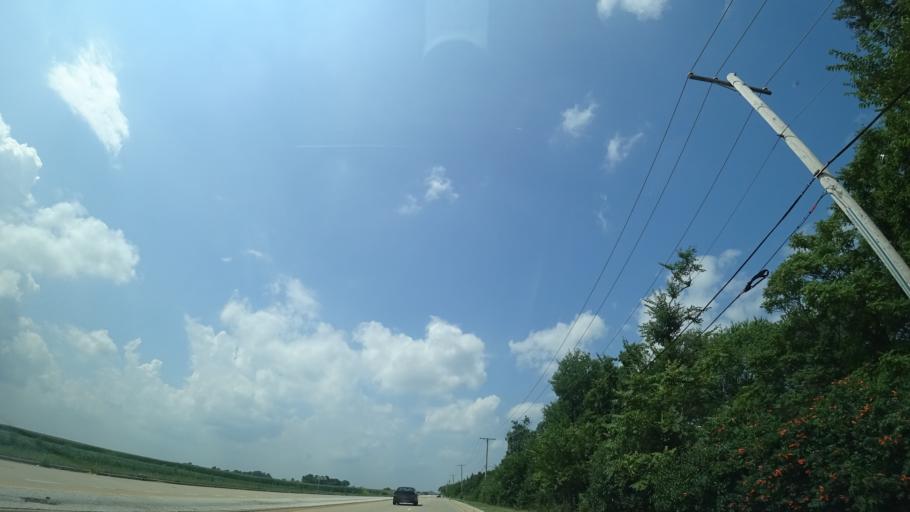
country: US
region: Illinois
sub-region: Will County
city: Frankfort Square
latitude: 41.5272
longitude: -87.7725
